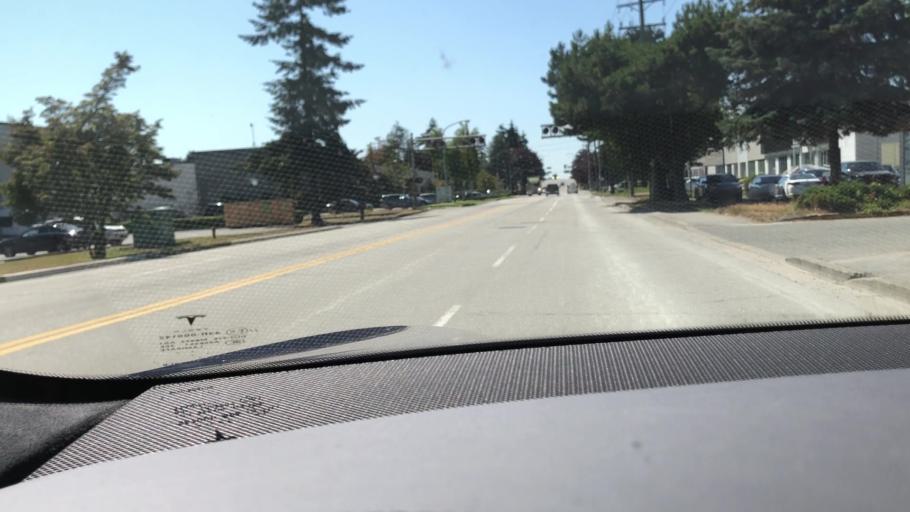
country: CA
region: British Columbia
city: Richmond
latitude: 49.1920
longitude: -123.0707
